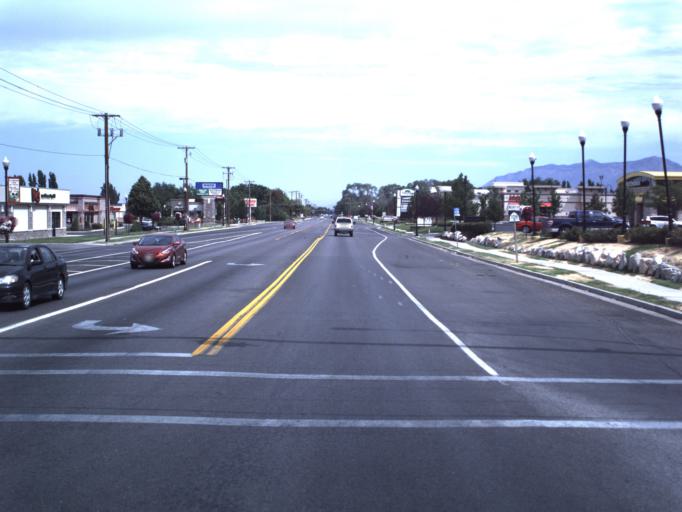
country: US
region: Utah
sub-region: Davis County
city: Clinton
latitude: 41.1399
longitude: -112.0644
